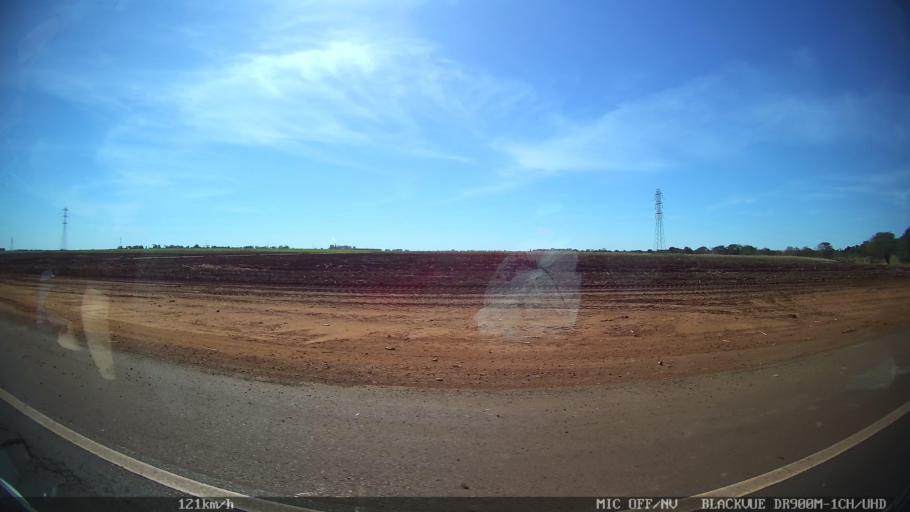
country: BR
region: Sao Paulo
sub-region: Guaira
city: Guaira
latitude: -20.4472
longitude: -48.2064
